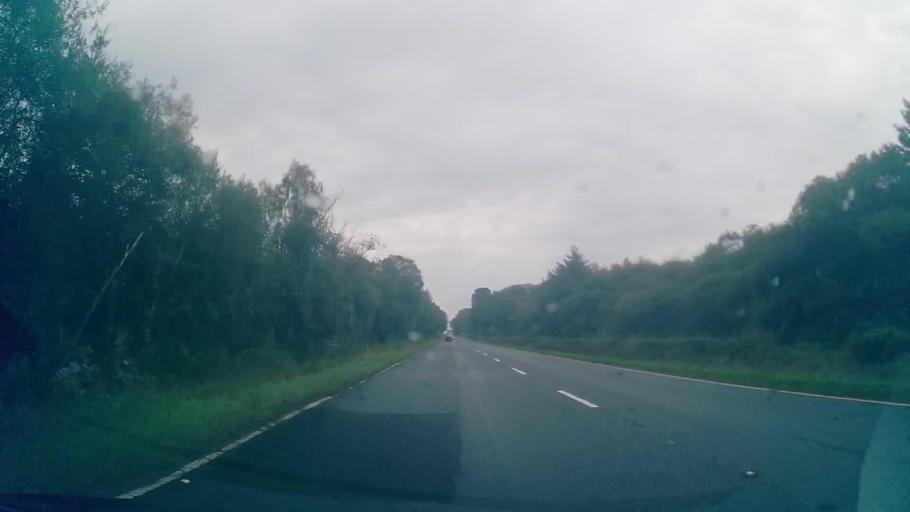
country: GB
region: Scotland
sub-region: Dumfries and Galloway
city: Annan
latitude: 55.0101
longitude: -3.3424
